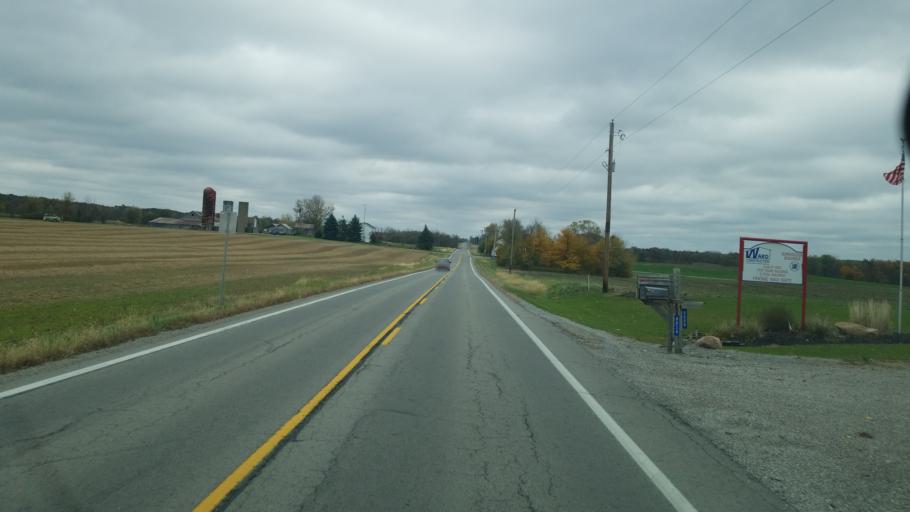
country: US
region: Ohio
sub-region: Seneca County
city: Tiffin
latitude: 41.0812
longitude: -82.9993
